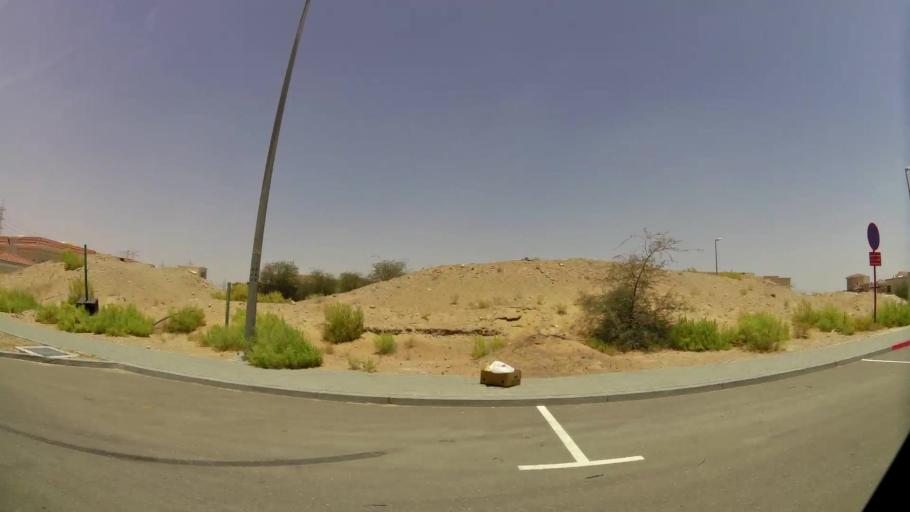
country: OM
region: Al Buraimi
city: Al Buraymi
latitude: 24.2708
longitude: 55.7099
